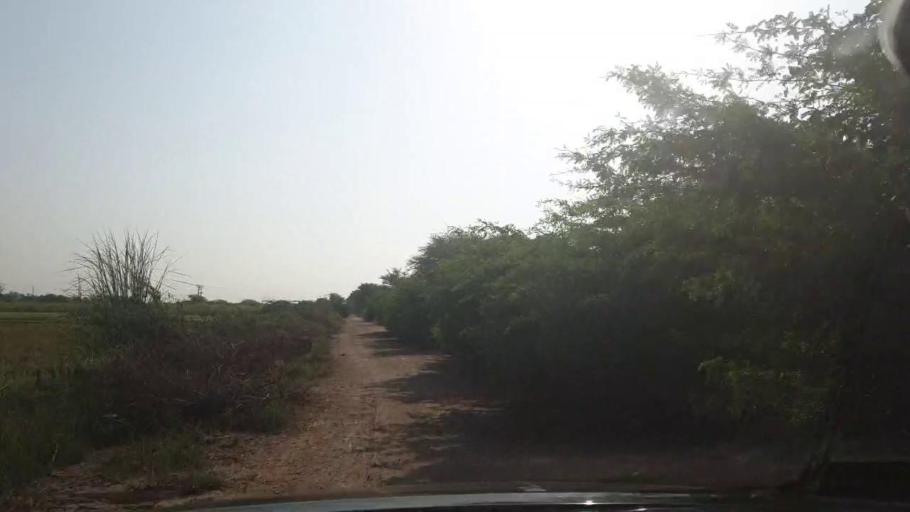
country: PK
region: Sindh
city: Tando Bago
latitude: 24.6509
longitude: 69.1668
